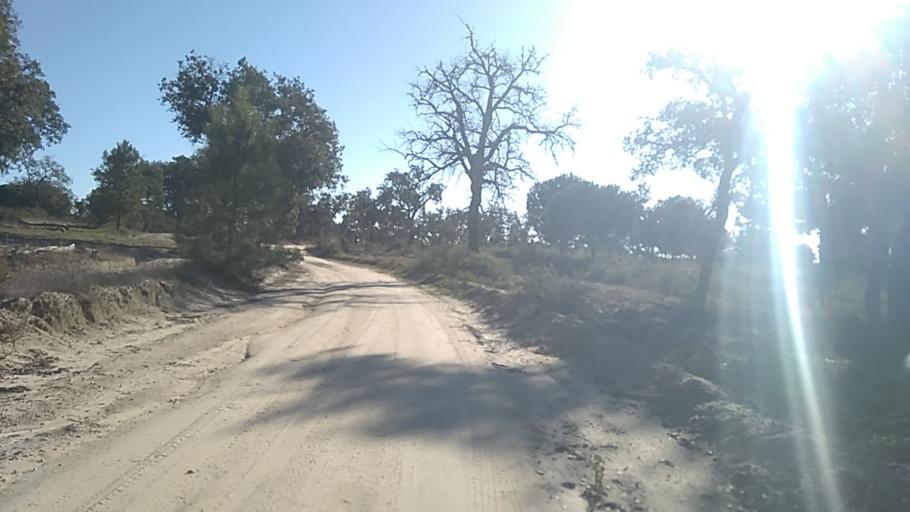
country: PT
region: Santarem
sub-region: Coruche
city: Coruche
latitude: 38.8579
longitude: -8.5265
